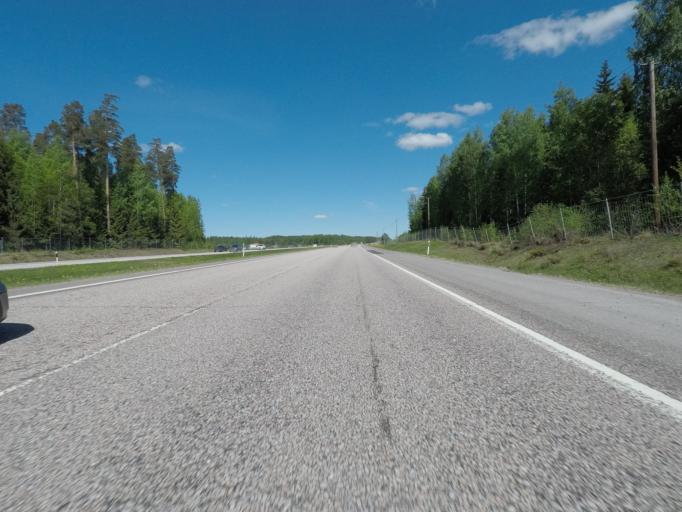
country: FI
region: Uusimaa
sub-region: Helsinki
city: Nurmijaervi
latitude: 60.4753
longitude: 24.8496
